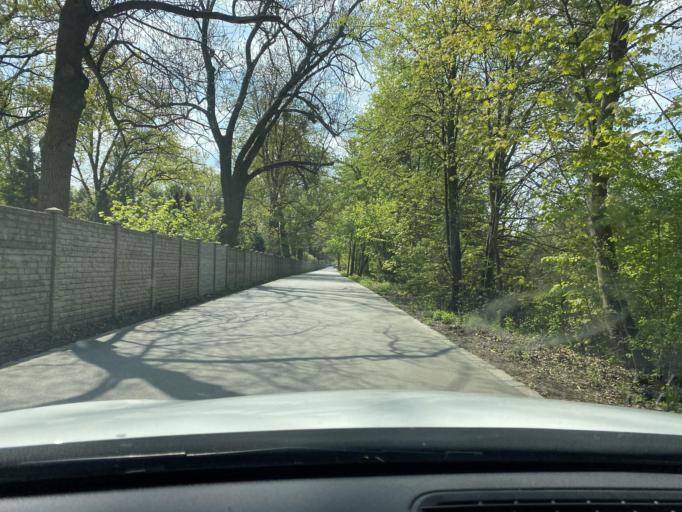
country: PL
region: Lower Silesian Voivodeship
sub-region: Powiat wroclawski
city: Wroclaw
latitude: 51.1390
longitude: 17.0058
